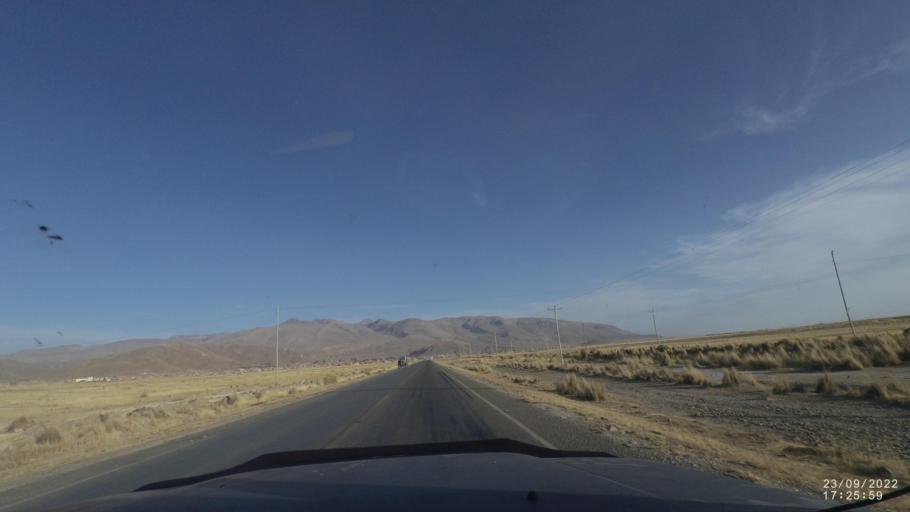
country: BO
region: Oruro
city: Challapata
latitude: -18.8785
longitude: -66.7909
